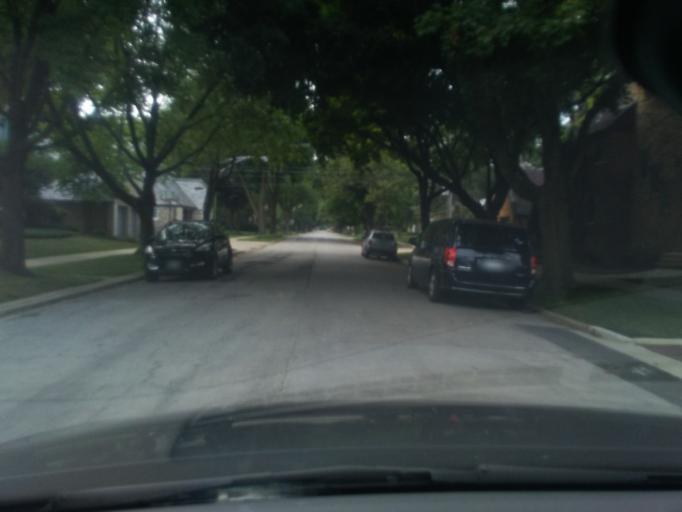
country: US
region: Illinois
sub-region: Cook County
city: Lincolnwood
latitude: 41.9922
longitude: -87.7420
